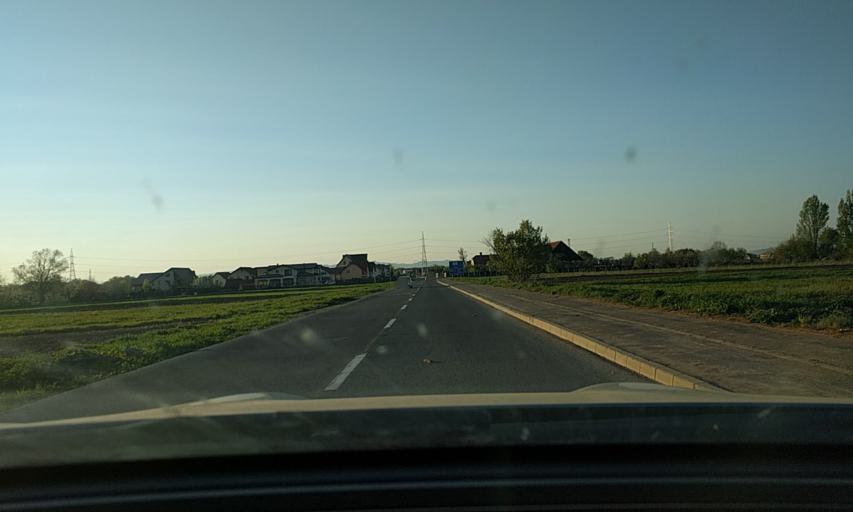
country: RO
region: Brasov
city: Brasov
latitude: 45.6842
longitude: 25.5707
